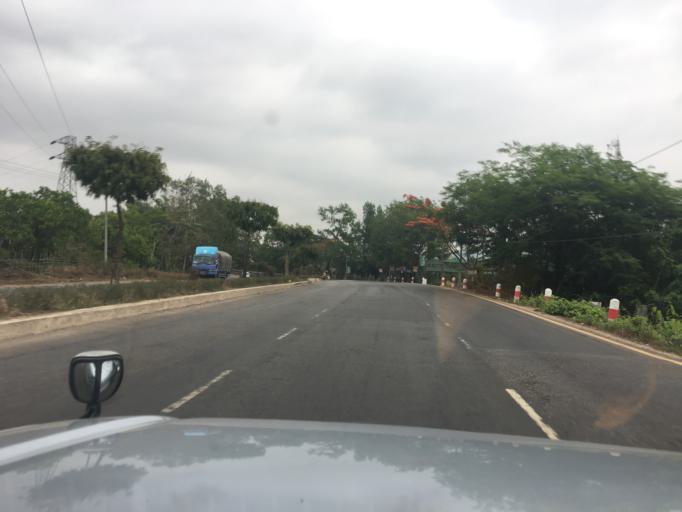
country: MM
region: Bago
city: Thanatpin
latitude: 17.2010
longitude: 96.4086
